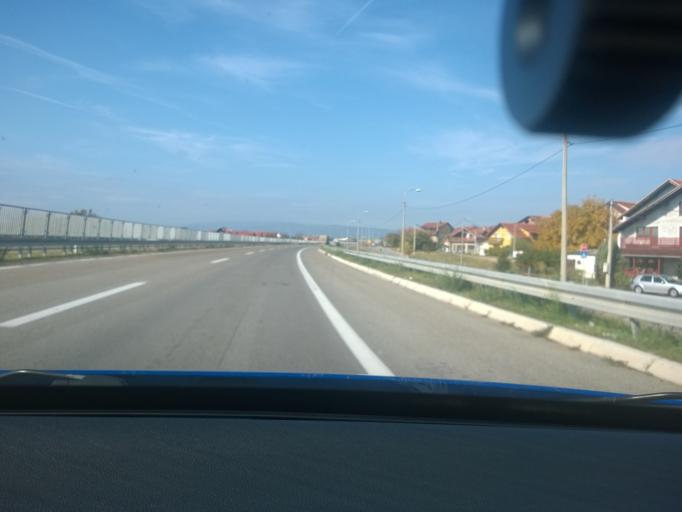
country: RS
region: Central Serbia
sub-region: Nisavski Okrug
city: Nis
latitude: 43.3427
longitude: 21.8859
